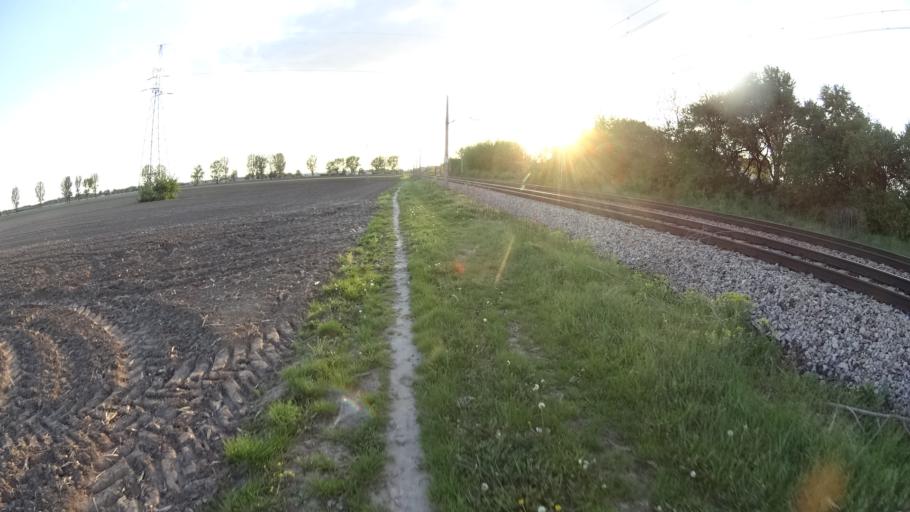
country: PL
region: Masovian Voivodeship
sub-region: Powiat pruszkowski
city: Piastow
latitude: 52.2066
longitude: 20.8266
